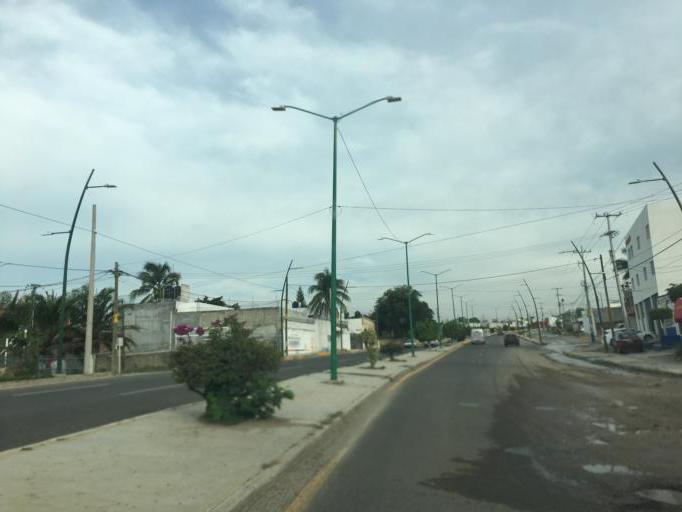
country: MX
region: Chiapas
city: Tuxtla Gutierrez
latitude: 16.7665
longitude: -93.1679
